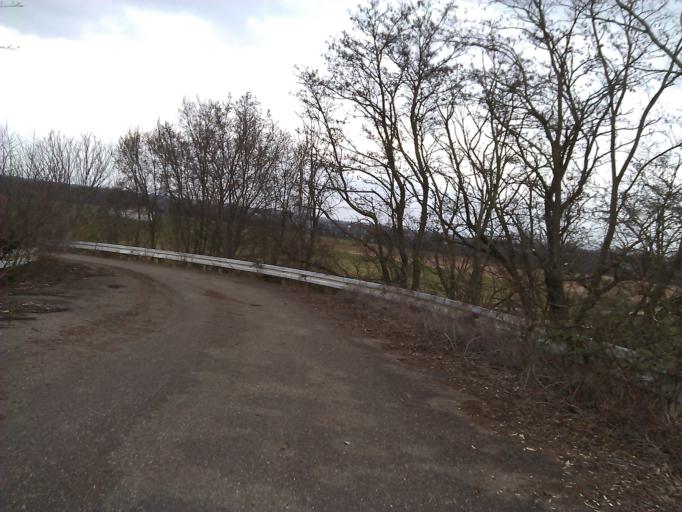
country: DE
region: Hesse
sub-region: Regierungsbezirk Darmstadt
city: Bischofsheim
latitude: 49.9849
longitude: 8.3773
